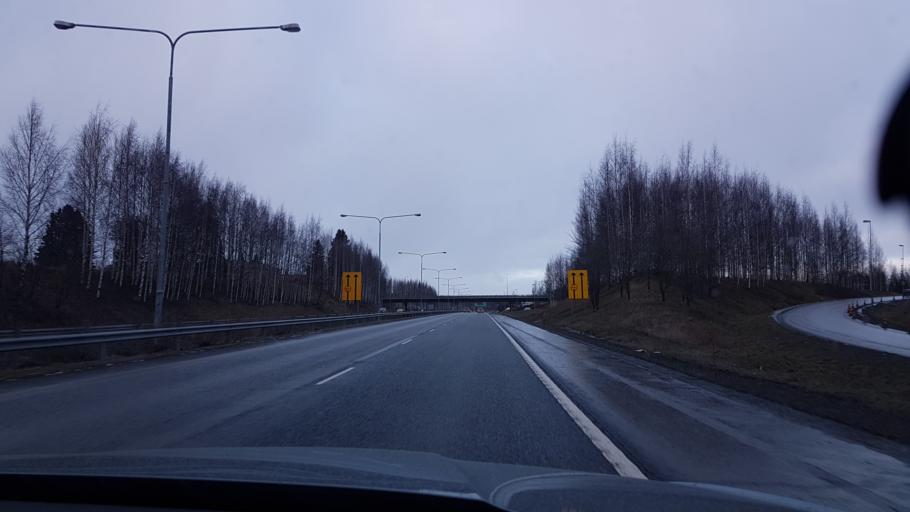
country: FI
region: Pirkanmaa
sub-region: Tampere
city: Tampere
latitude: 61.4855
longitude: 23.8740
